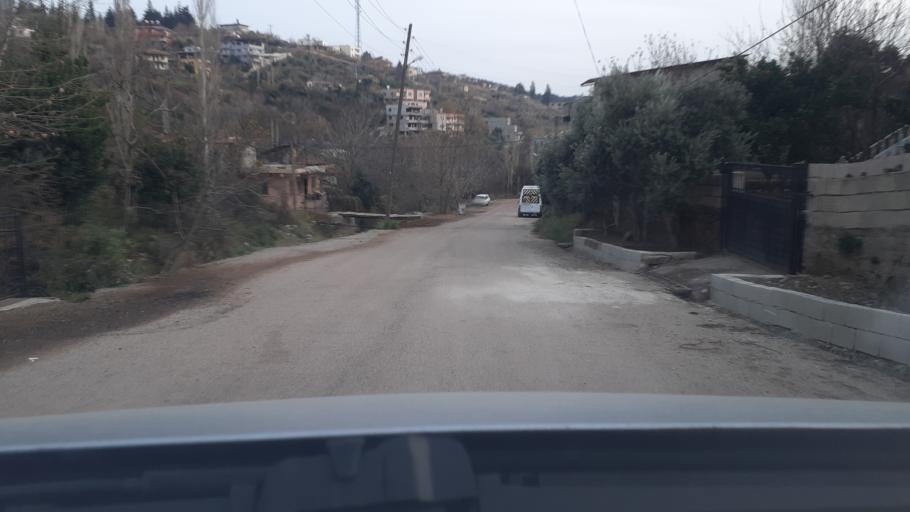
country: TR
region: Hatay
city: Kirikhan
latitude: 36.5366
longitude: 36.3133
